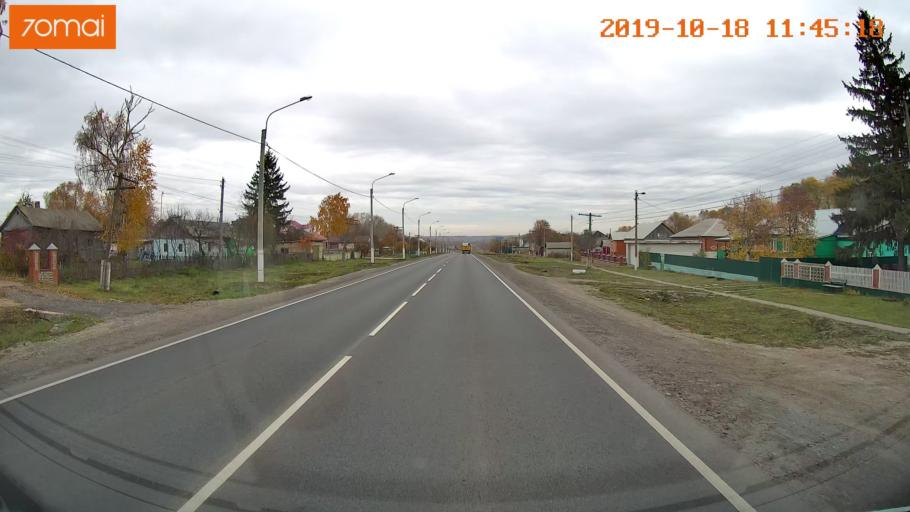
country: RU
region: Rjazan
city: Mikhaylov
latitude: 54.2095
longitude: 38.9685
